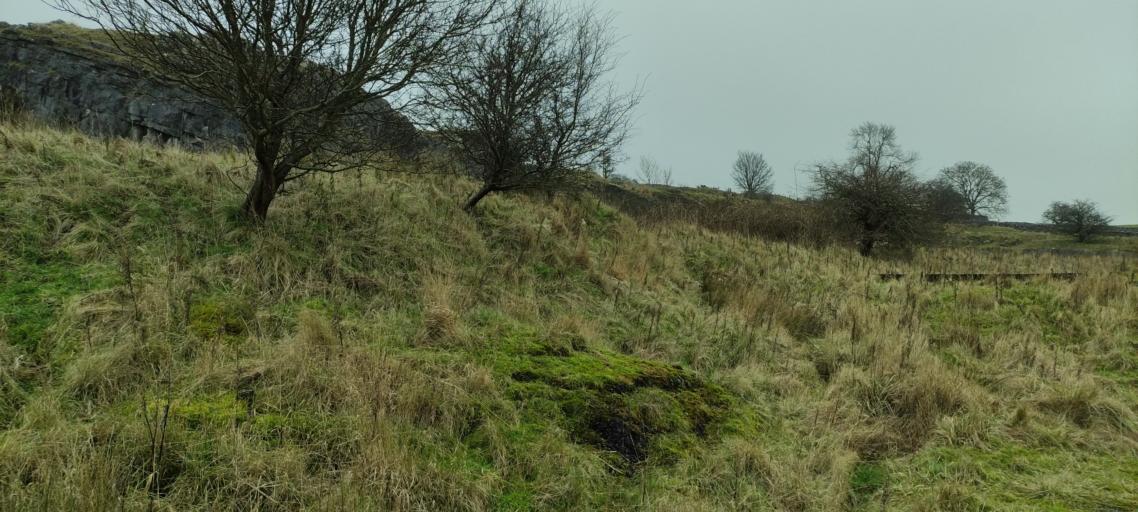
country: GB
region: England
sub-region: North Yorkshire
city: Ingleton
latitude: 54.1565
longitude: -2.4617
